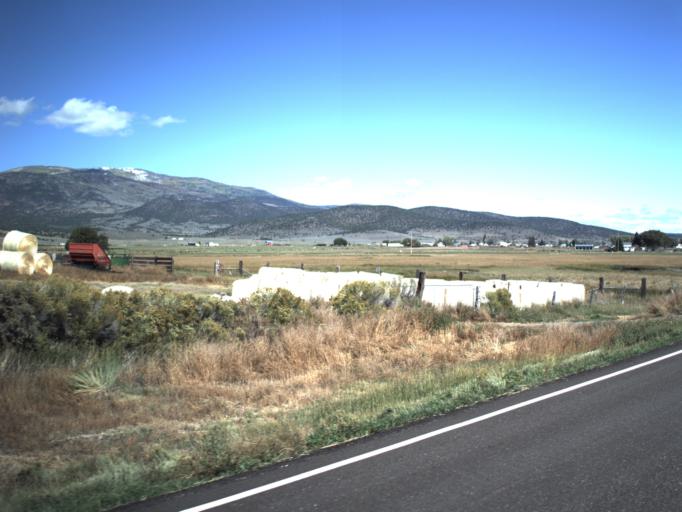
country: US
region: Utah
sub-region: Wayne County
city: Loa
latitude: 38.4929
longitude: -111.8821
